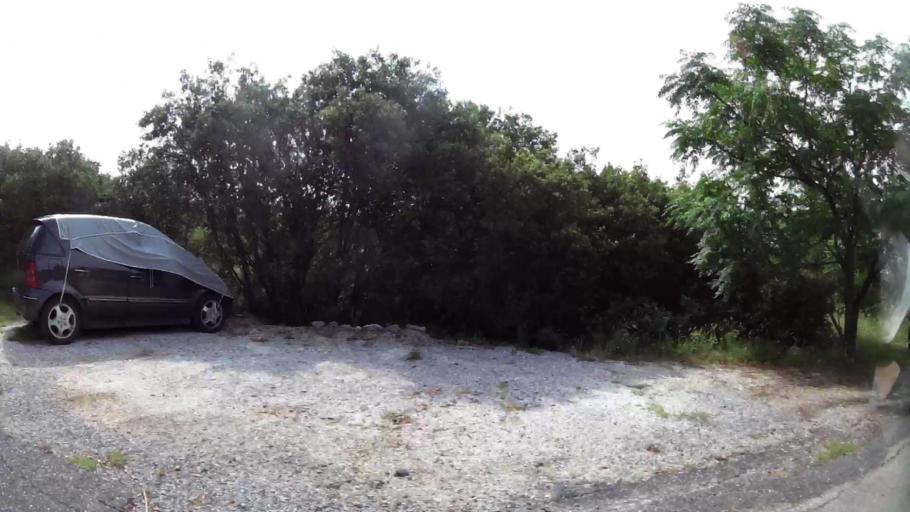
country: GR
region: Central Macedonia
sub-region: Nomos Thessalonikis
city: Panorama
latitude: 40.5792
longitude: 23.0078
